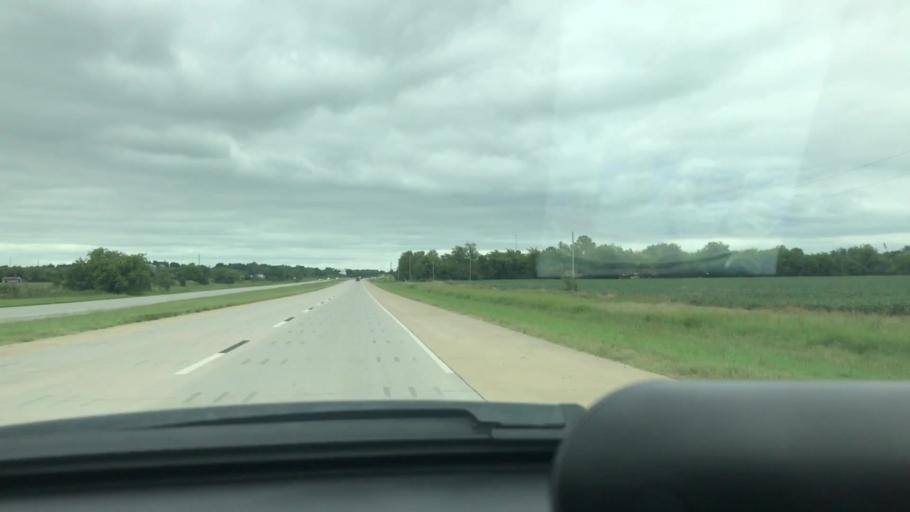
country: US
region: Oklahoma
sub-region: Mayes County
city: Chouteau
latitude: 36.0900
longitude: -95.3632
